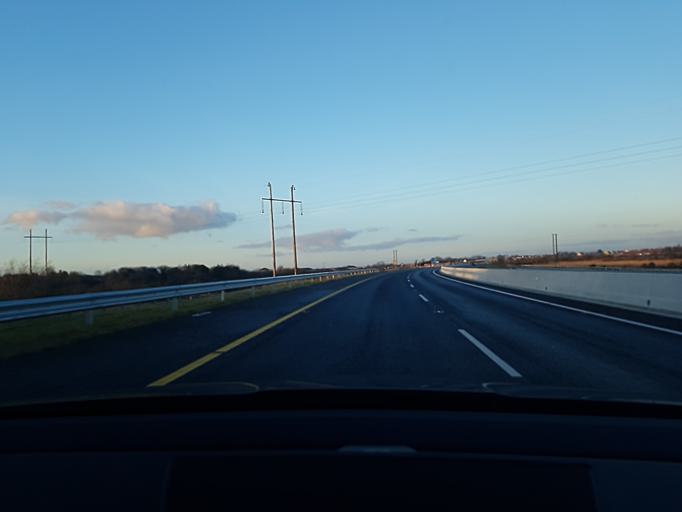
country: IE
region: Connaught
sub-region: County Galway
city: Tuam
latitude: 53.4994
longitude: -8.8786
